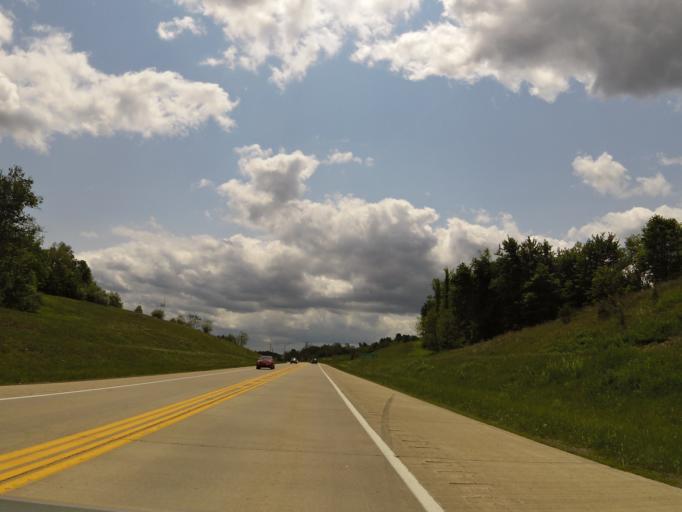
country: US
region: Ohio
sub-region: Athens County
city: Athens
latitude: 39.2411
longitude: -82.0759
